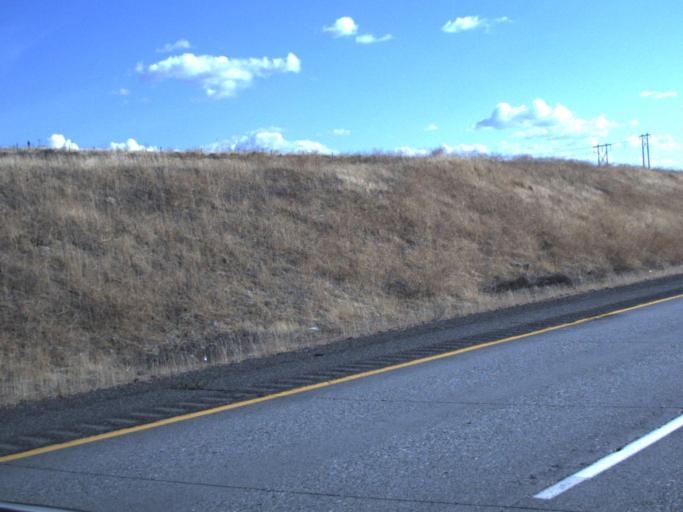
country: US
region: Washington
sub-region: Benton County
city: Highland
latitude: 46.0548
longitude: -119.2243
